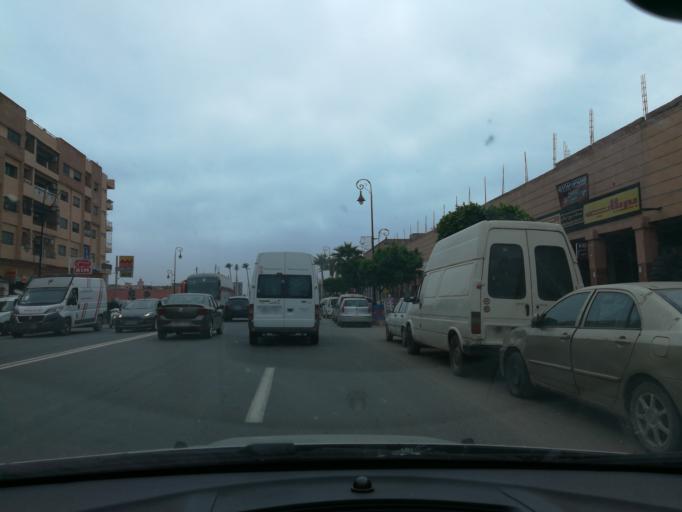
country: MA
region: Marrakech-Tensift-Al Haouz
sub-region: Marrakech
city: Marrakesh
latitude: 31.6459
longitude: -7.9788
